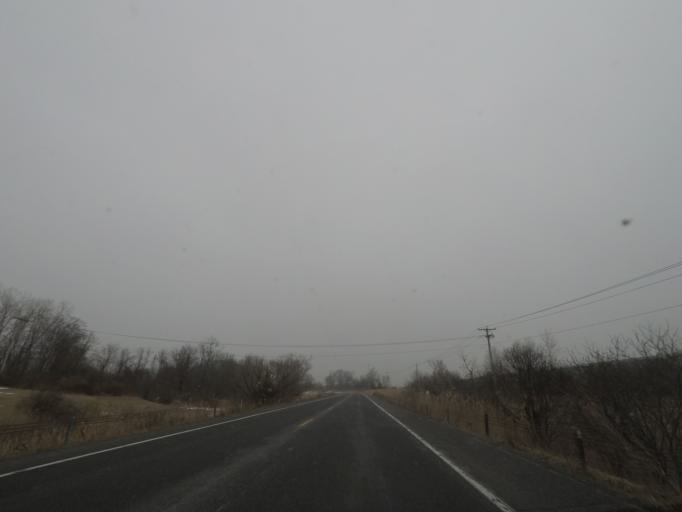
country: US
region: New York
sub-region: Albany County
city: Delmar
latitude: 42.5694
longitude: -73.8538
